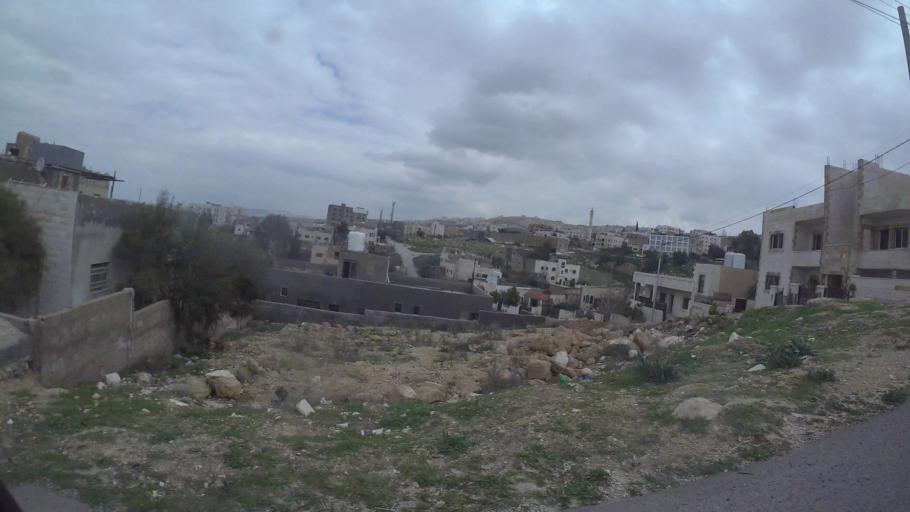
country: JO
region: Amman
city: Al Jubayhah
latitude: 32.0493
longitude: 35.8414
